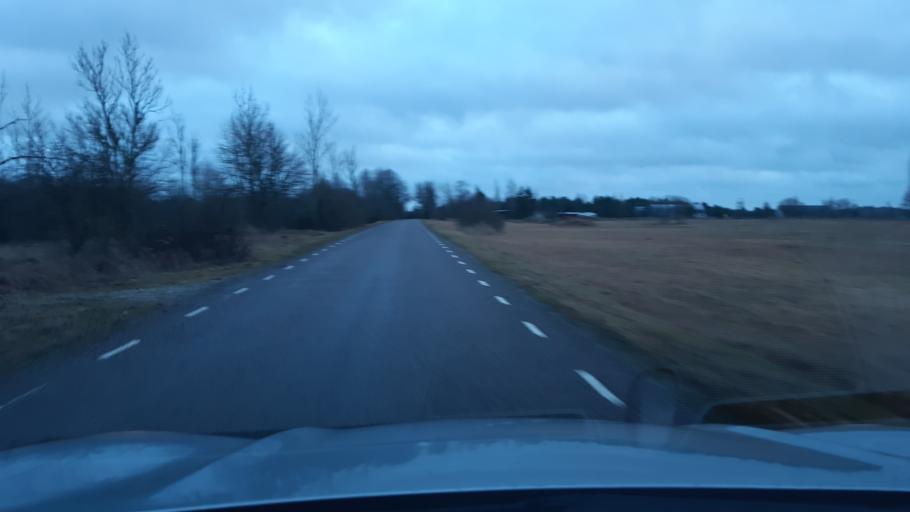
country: EE
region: Raplamaa
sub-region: Rapla vald
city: Rapla
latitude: 58.9894
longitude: 24.7272
